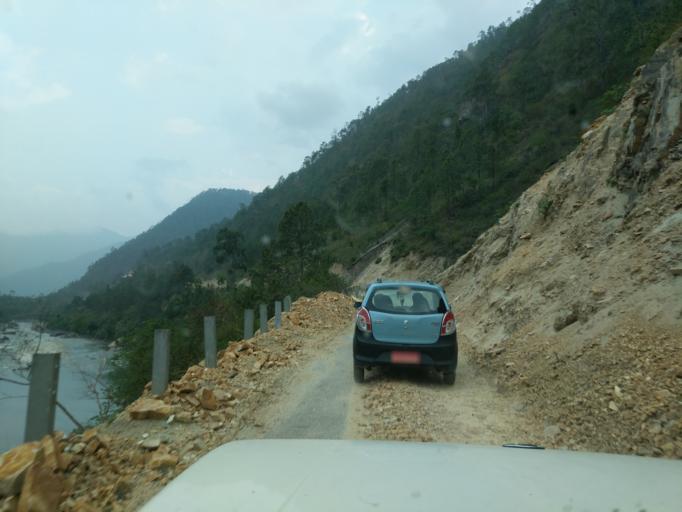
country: BT
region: Mongar
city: Mongar
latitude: 27.2725
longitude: 91.1918
